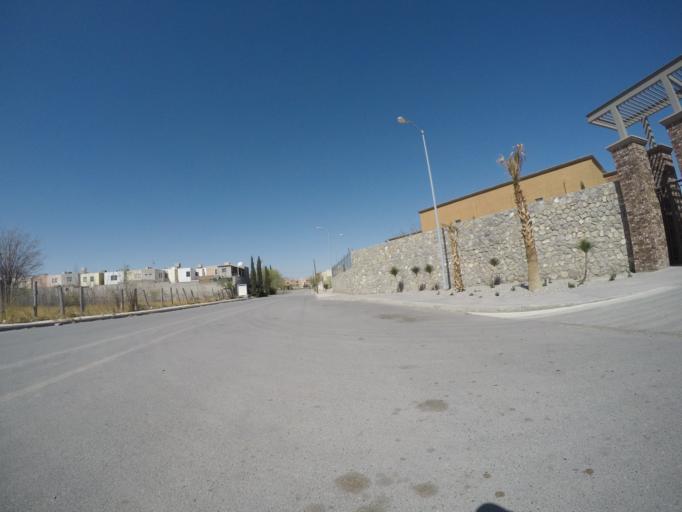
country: MX
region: Chihuahua
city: Ciudad Juarez
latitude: 31.6935
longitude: -106.4134
